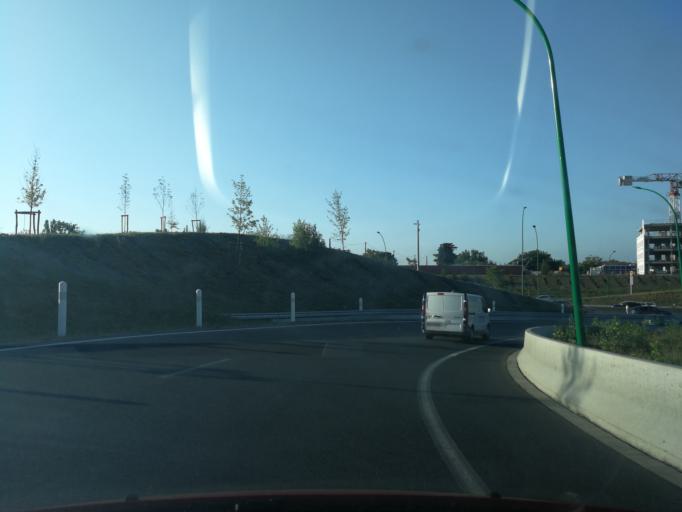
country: FR
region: Midi-Pyrenees
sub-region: Departement de la Haute-Garonne
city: L'Union
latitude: 43.6476
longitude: 1.4562
